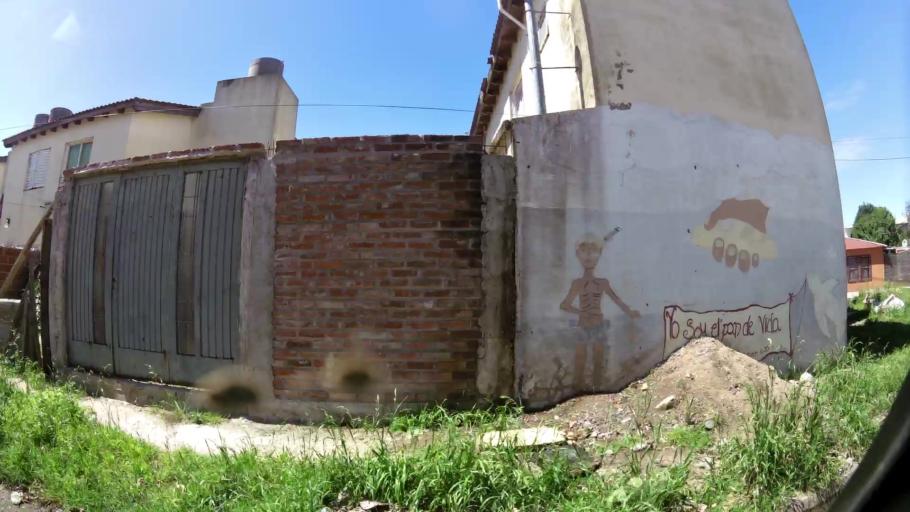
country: AR
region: Buenos Aires
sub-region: Partido de Lanus
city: Lanus
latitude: -34.7382
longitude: -58.3448
